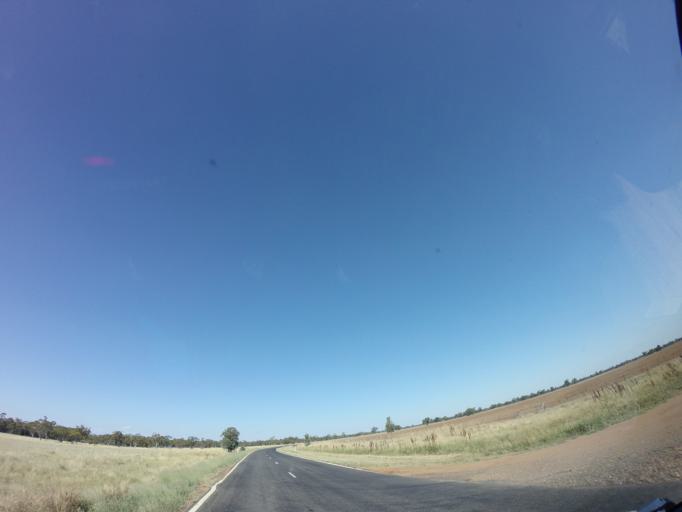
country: AU
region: New South Wales
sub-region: Gilgandra
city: Gilgandra
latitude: -31.6682
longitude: 148.2147
